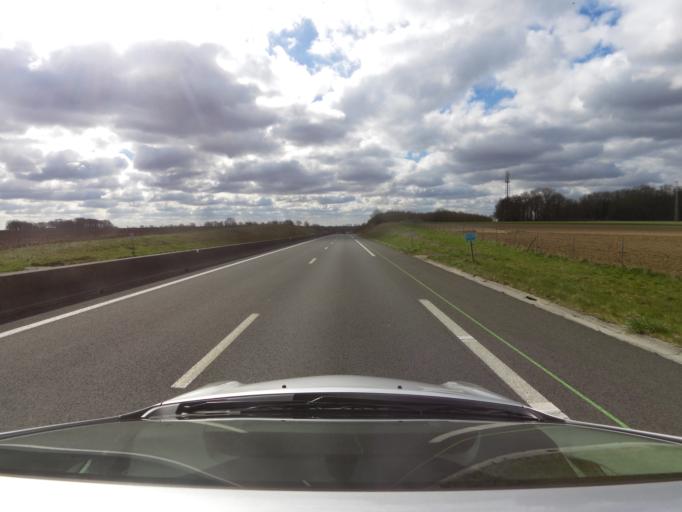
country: FR
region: Picardie
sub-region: Departement de la Somme
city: Rue
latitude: 50.2820
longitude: 1.7328
